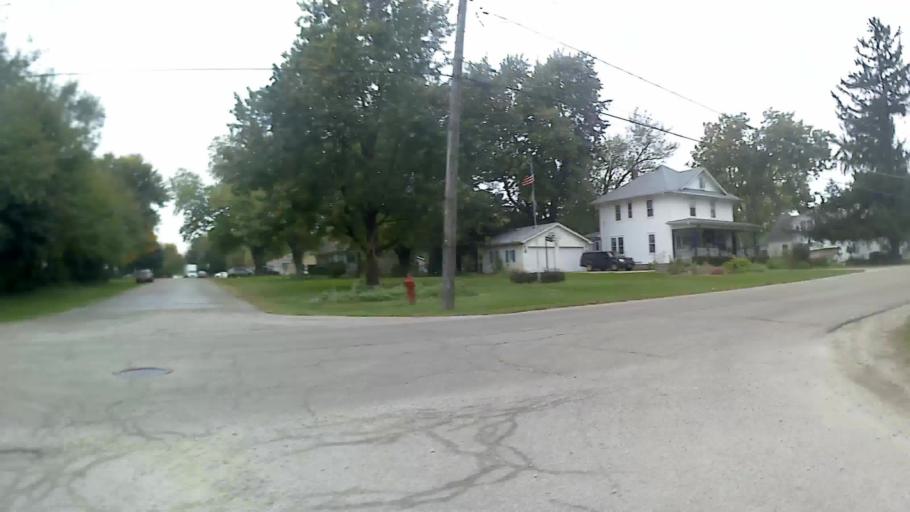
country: US
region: Illinois
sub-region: Kane County
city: Montgomery
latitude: 41.7474
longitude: -88.3445
